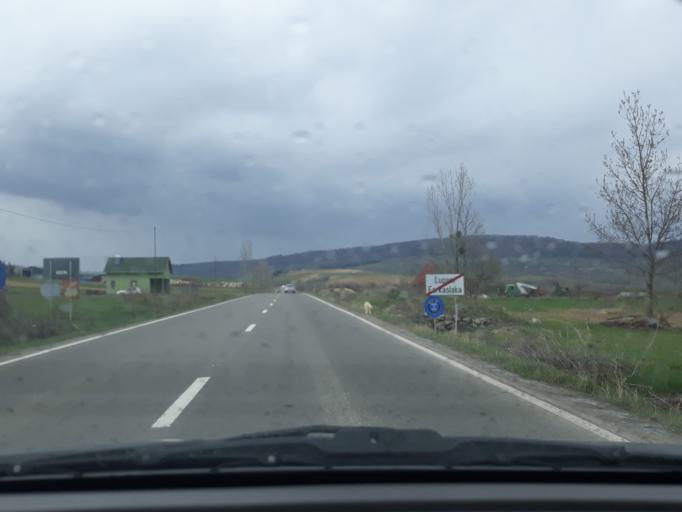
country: RO
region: Harghita
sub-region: Comuna Lupeni
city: Lupeni
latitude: 46.3866
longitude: 25.2173
